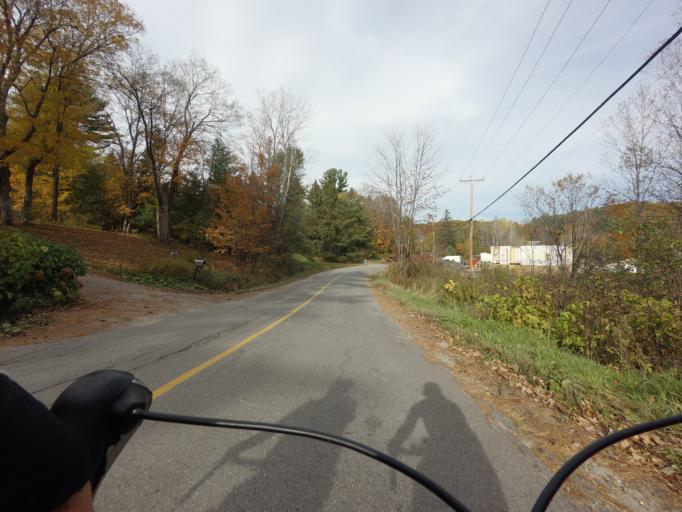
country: CA
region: Quebec
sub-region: Outaouais
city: Val-des-Monts
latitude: 45.5655
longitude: -75.6620
